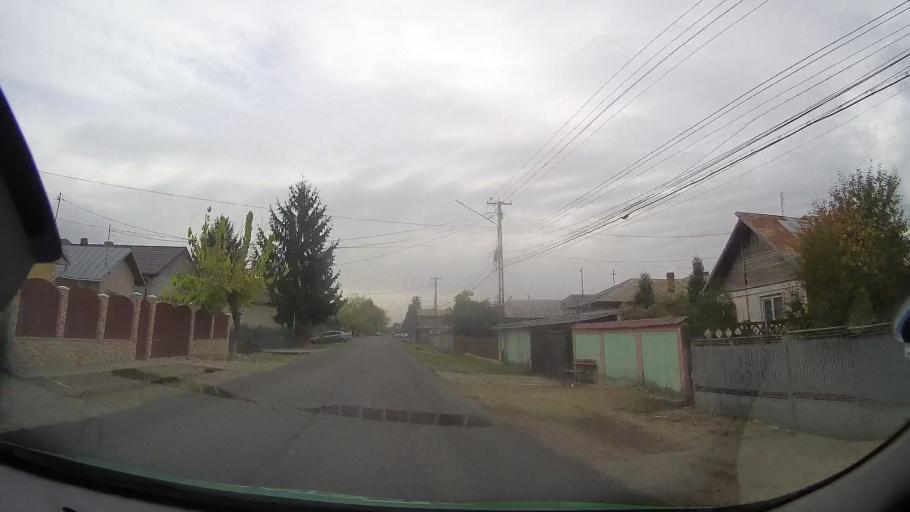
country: RO
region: Prahova
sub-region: Comuna Valea Calugareasca
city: Pantazi
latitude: 44.9367
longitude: 26.1378
